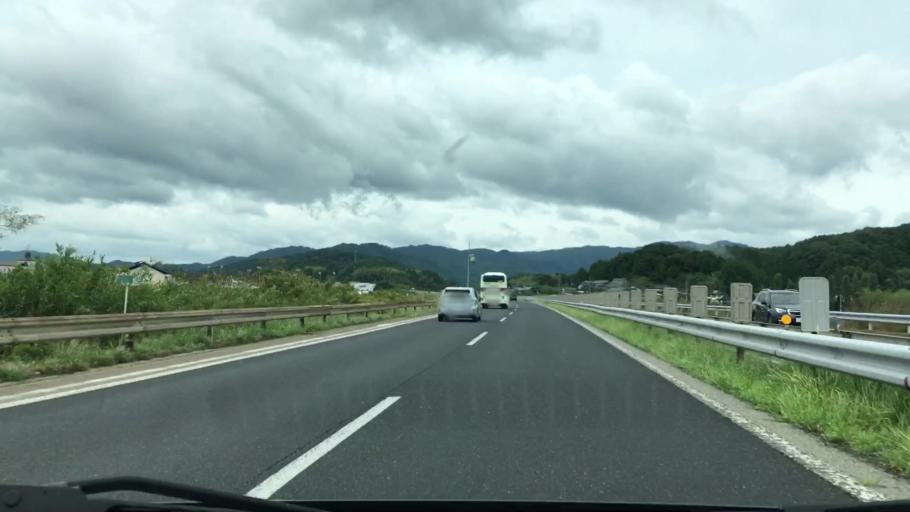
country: JP
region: Okayama
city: Tsuyama
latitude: 35.0595
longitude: 133.9078
